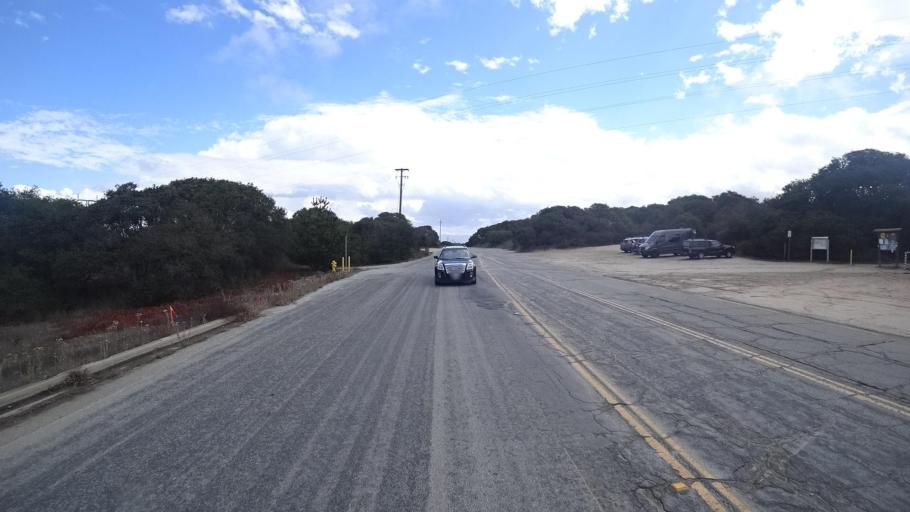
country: US
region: California
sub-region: Monterey County
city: Marina
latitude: 36.6552
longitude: -121.7578
